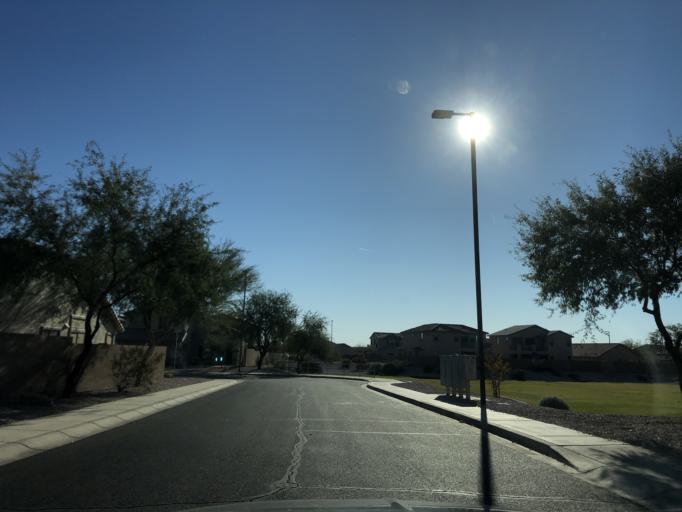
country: US
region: Arizona
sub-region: Maricopa County
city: Buckeye
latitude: 33.4258
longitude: -112.6058
